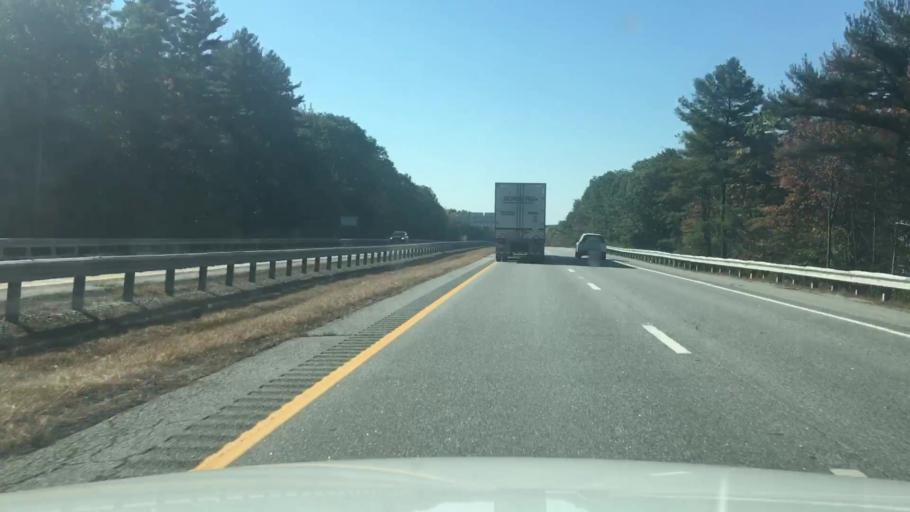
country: US
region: Maine
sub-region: Cumberland County
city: Falmouth
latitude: 43.7320
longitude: -70.2643
